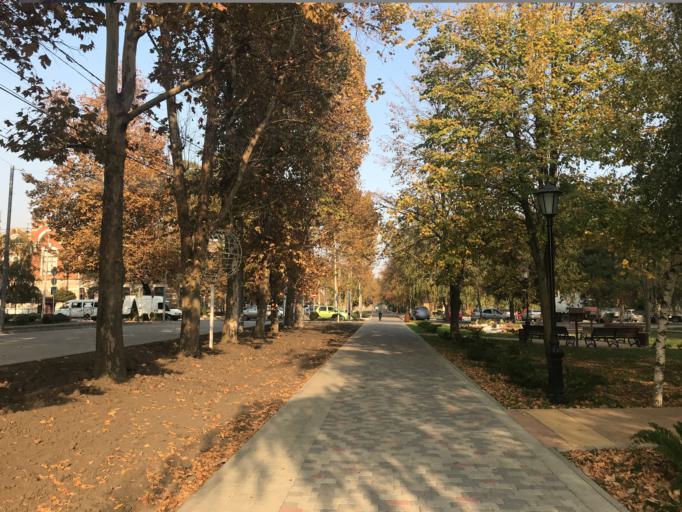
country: RU
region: Krasnodarskiy
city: Slavyansk-na-Kubani
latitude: 45.2604
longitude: 38.1293
